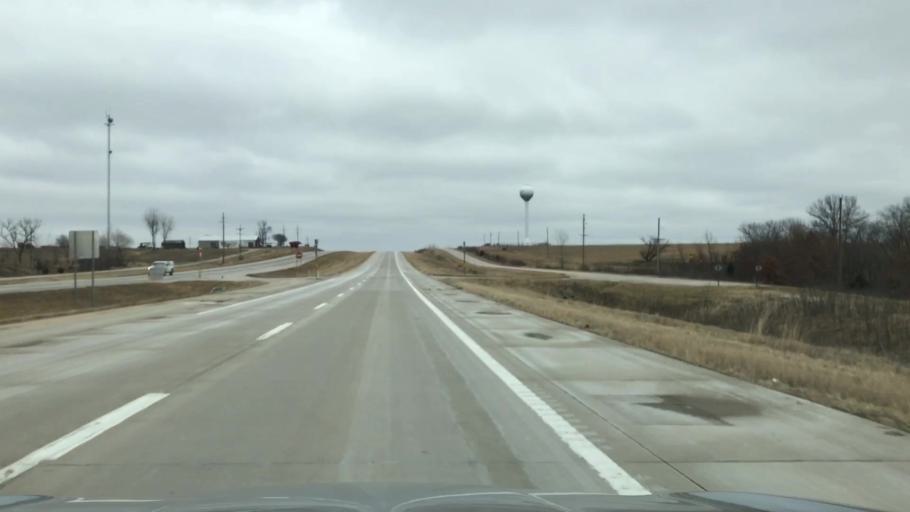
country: US
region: Missouri
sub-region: Livingston County
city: Chillicothe
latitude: 39.7392
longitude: -93.6645
